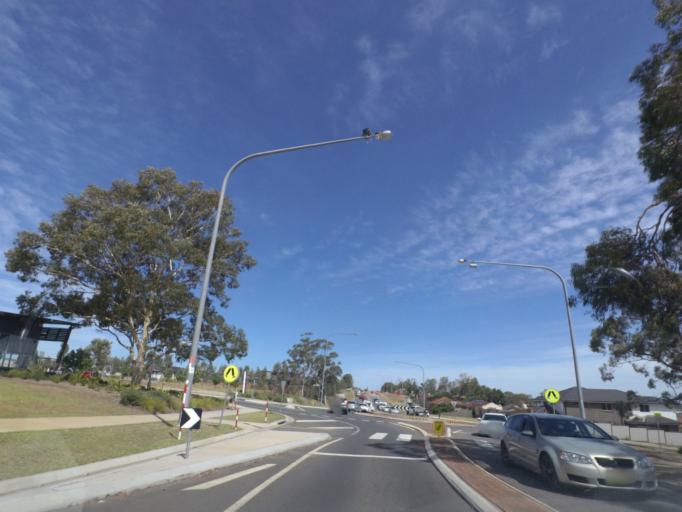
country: AU
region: New South Wales
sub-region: Campbelltown Municipality
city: Campbelltown
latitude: -34.0481
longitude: 150.8038
